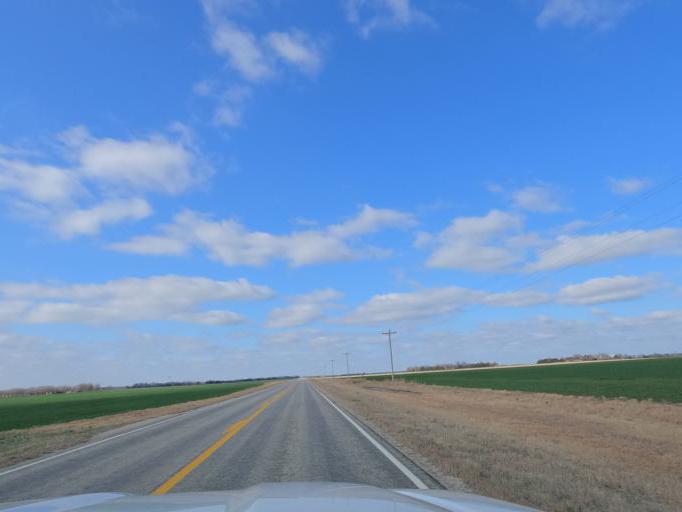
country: US
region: Kansas
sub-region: McPherson County
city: Inman
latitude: 38.2238
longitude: -97.8485
